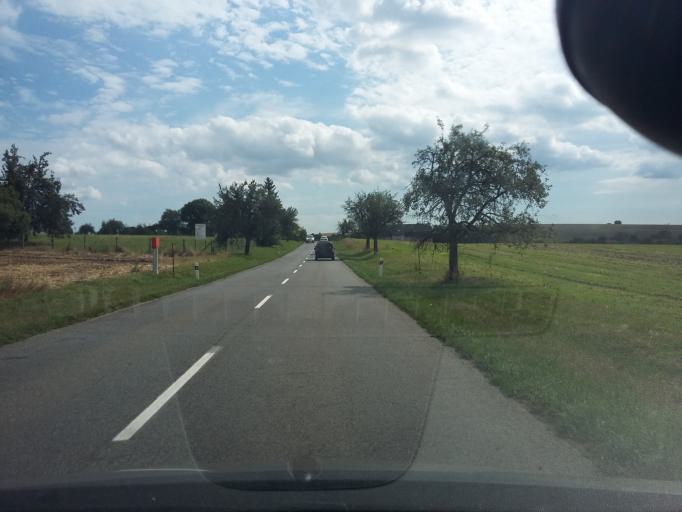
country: SK
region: Trnavsky
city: Gbely
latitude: 48.7284
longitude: 17.1630
